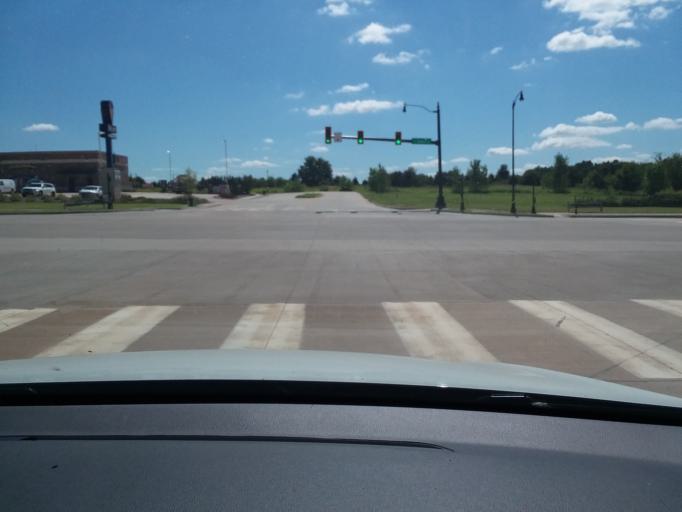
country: US
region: Oklahoma
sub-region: Oklahoma County
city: Edmond
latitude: 35.6820
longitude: -97.4206
